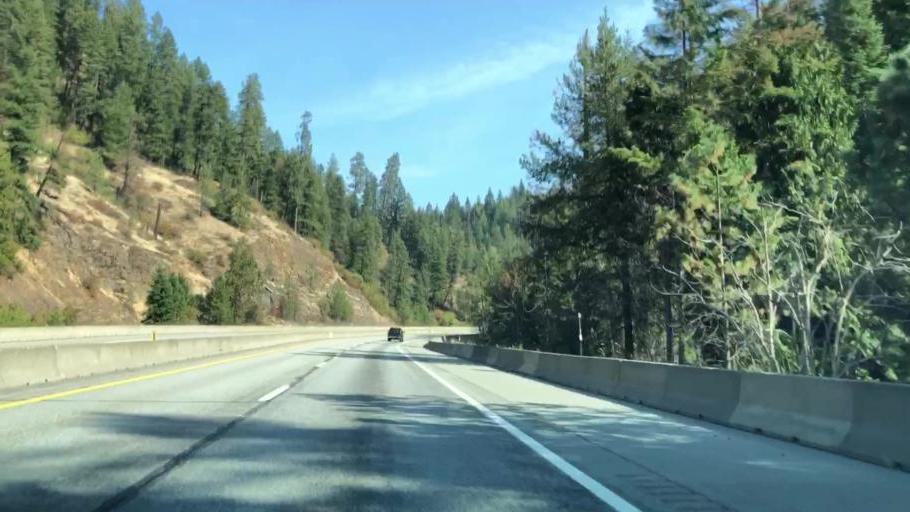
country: US
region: Idaho
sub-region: Kootenai County
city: Coeur d'Alene
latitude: 47.6268
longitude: -116.5915
